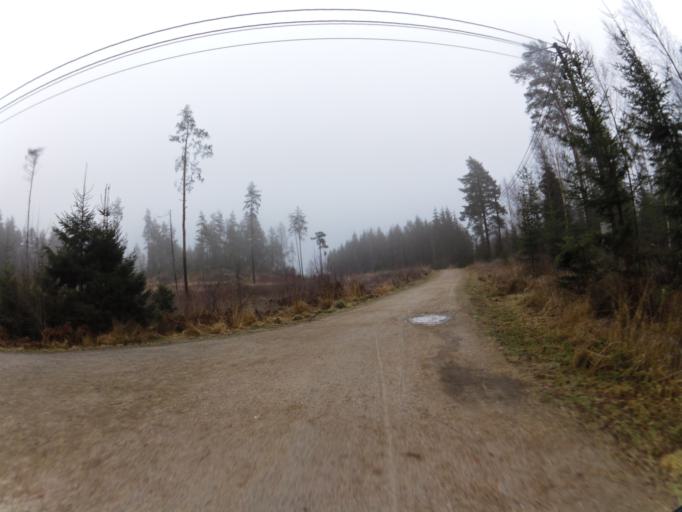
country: NO
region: Ostfold
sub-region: Fredrikstad
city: Fredrikstad
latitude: 59.2653
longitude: 10.9861
